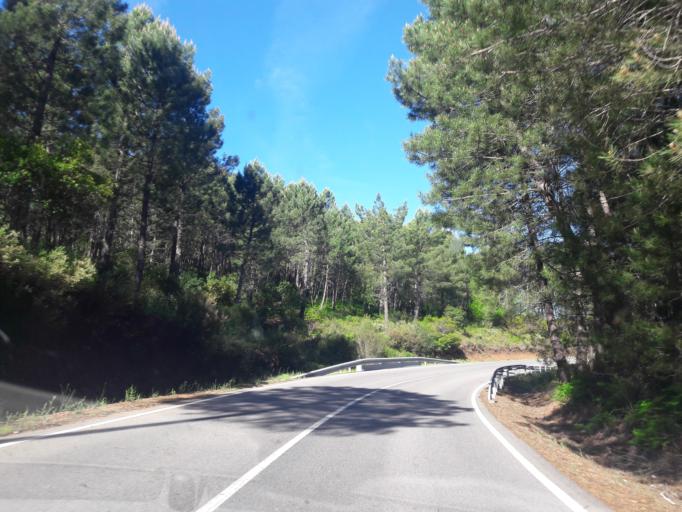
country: ES
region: Castille and Leon
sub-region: Provincia de Salamanca
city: Herguijuela de la Sierra
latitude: 40.4132
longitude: -6.1039
